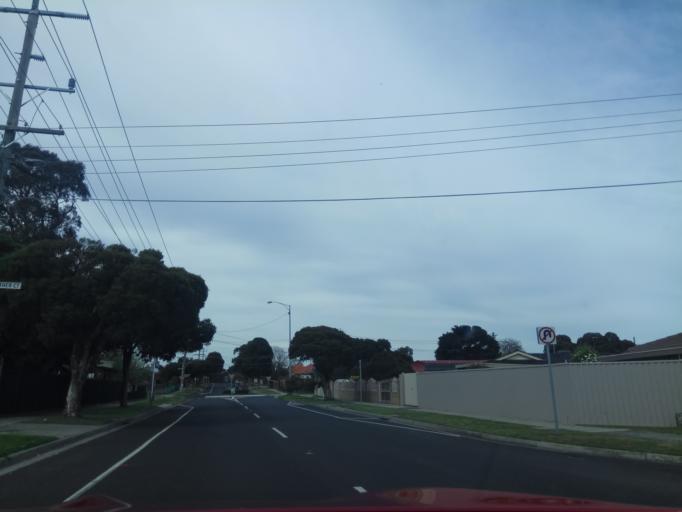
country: AU
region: Victoria
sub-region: Greater Dandenong
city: Springvale South
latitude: -37.9639
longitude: 145.1390
